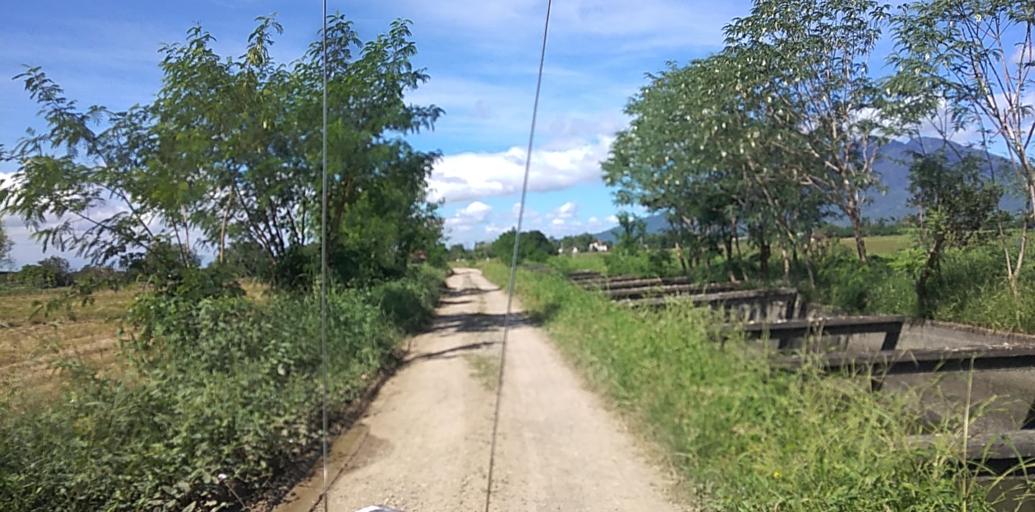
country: PH
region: Central Luzon
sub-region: Province of Pampanga
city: Candating
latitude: 15.1307
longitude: 120.7964
